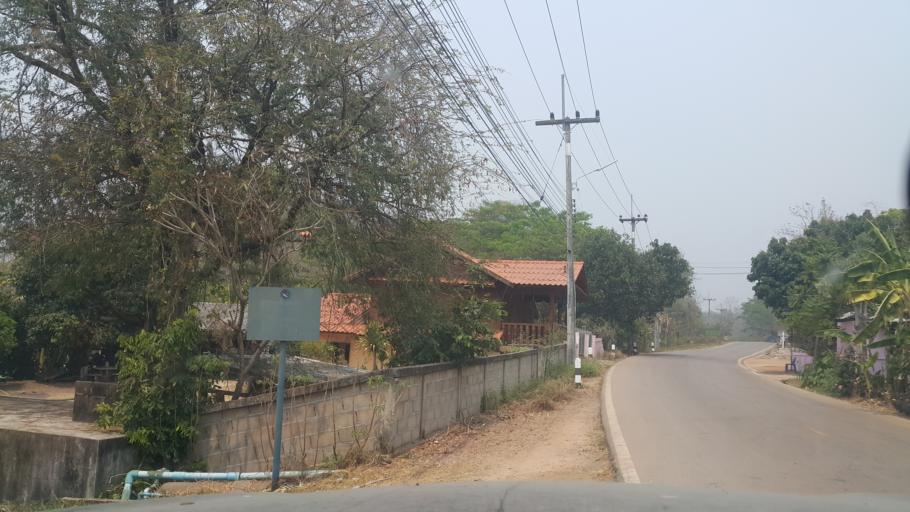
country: TH
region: Lampang
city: Soem Ngam
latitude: 18.1942
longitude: 99.1956
